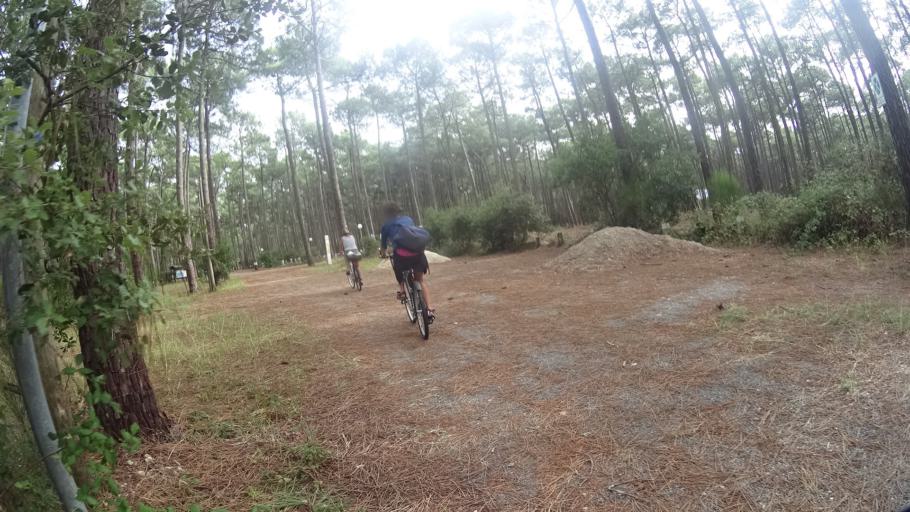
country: FR
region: Aquitaine
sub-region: Departement de la Gironde
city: Lacanau
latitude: 44.9881
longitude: -1.1375
